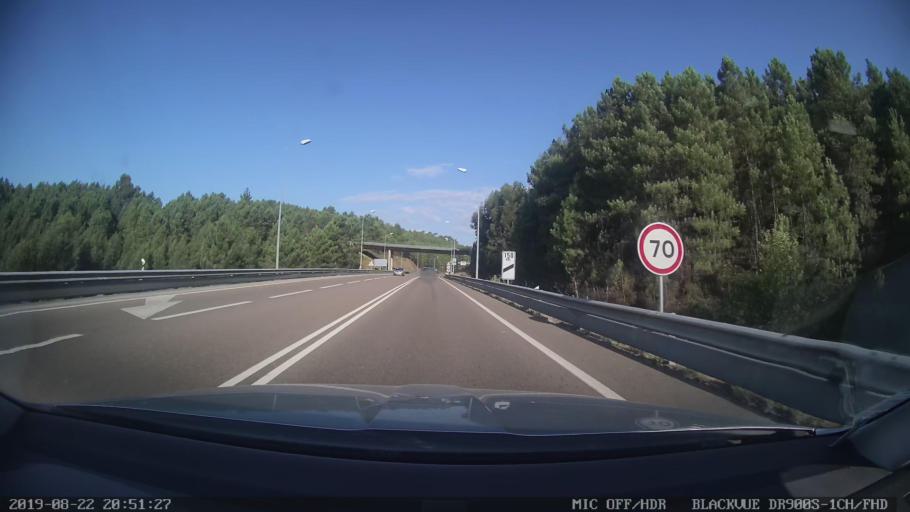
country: PT
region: Castelo Branco
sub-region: Proenca-A-Nova
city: Proenca-a-Nova
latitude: 39.7599
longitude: -7.9600
